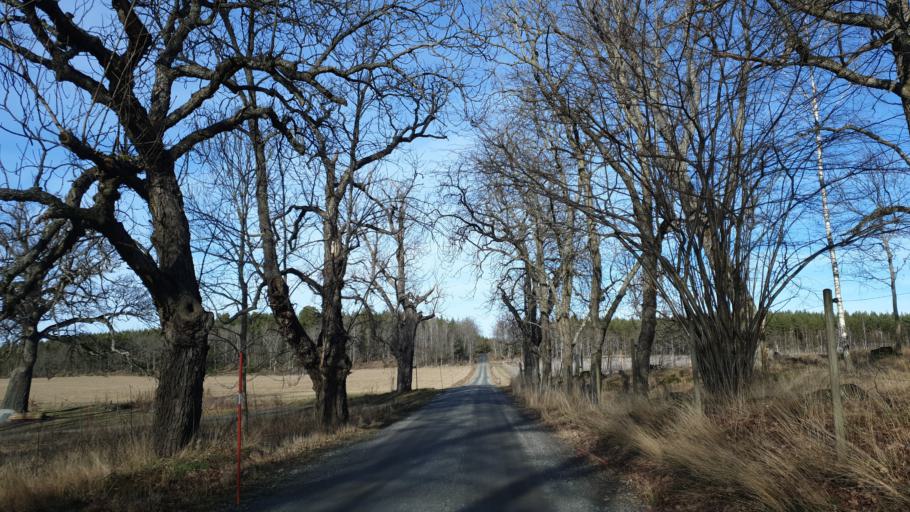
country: SE
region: Uppsala
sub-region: Enkopings Kommun
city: Dalby
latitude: 59.4756
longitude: 17.2511
